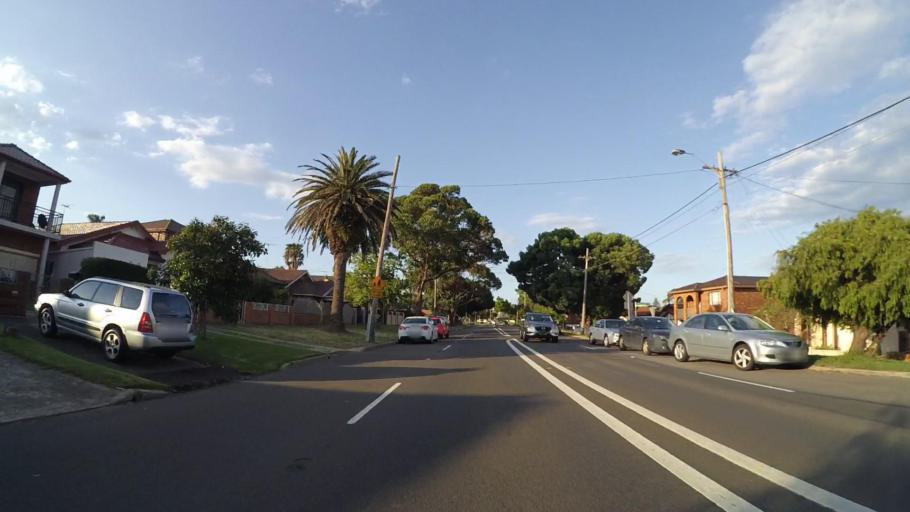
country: AU
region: New South Wales
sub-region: Randwick
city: Daceyville
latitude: -33.9367
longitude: 151.2298
